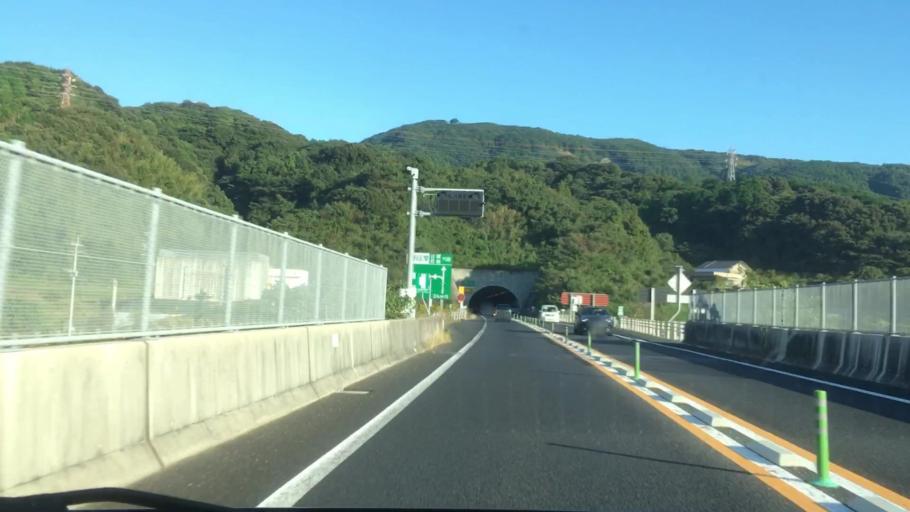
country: JP
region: Nagasaki
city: Sasebo
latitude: 33.1899
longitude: 129.6863
